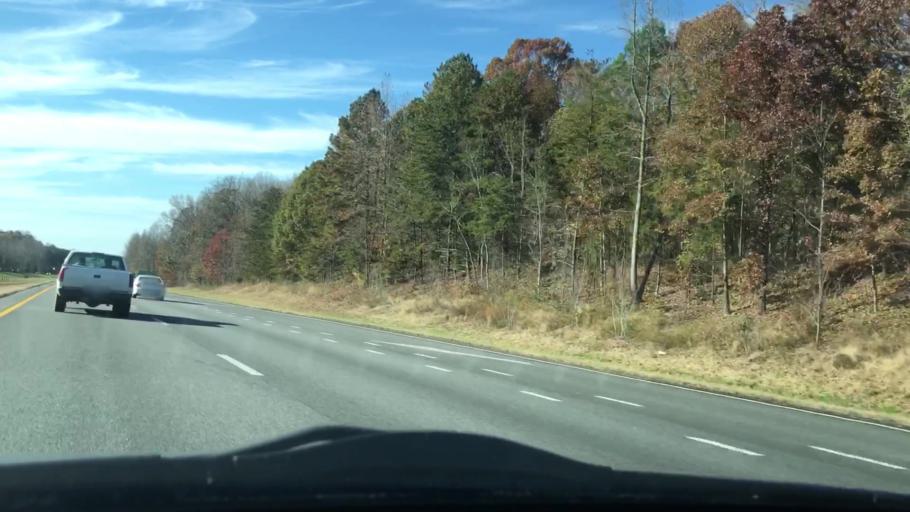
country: US
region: North Carolina
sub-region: Davidson County
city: Wallburg
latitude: 36.0284
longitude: -80.0640
